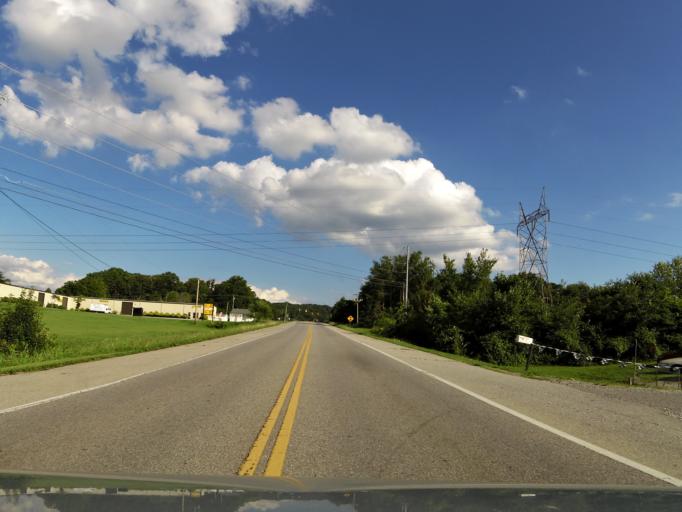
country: US
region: Tennessee
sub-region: Blount County
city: Maryville
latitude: 35.7319
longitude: -84.0339
